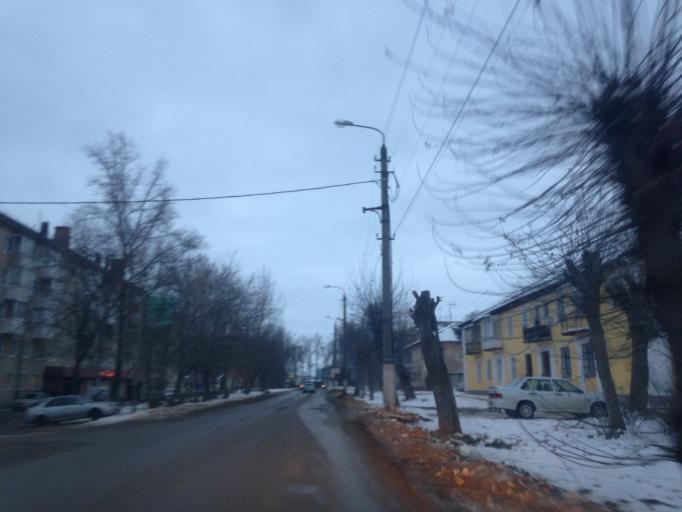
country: RU
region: Tula
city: Shchekino
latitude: 53.9996
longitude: 37.5270
